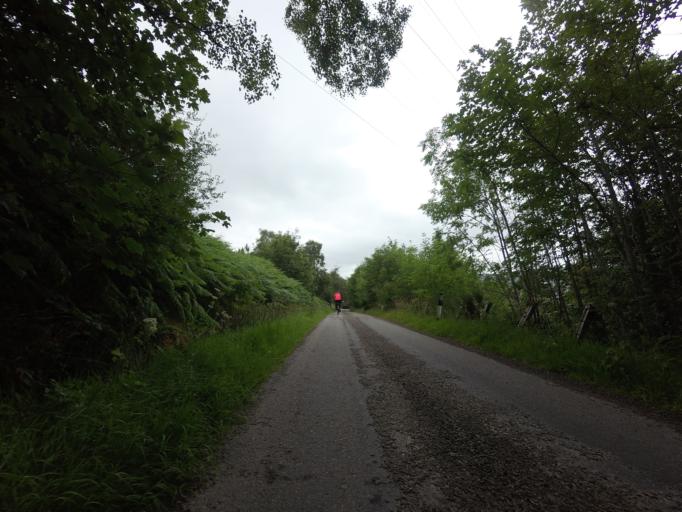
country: GB
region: Scotland
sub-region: Highland
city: Alness
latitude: 57.8942
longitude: -4.3755
